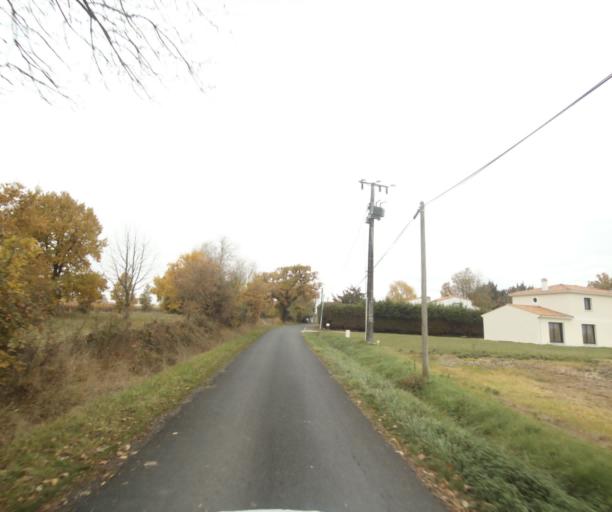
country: FR
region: Poitou-Charentes
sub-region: Departement de la Charente-Maritime
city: Chermignac
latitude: 45.7090
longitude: -0.6638
